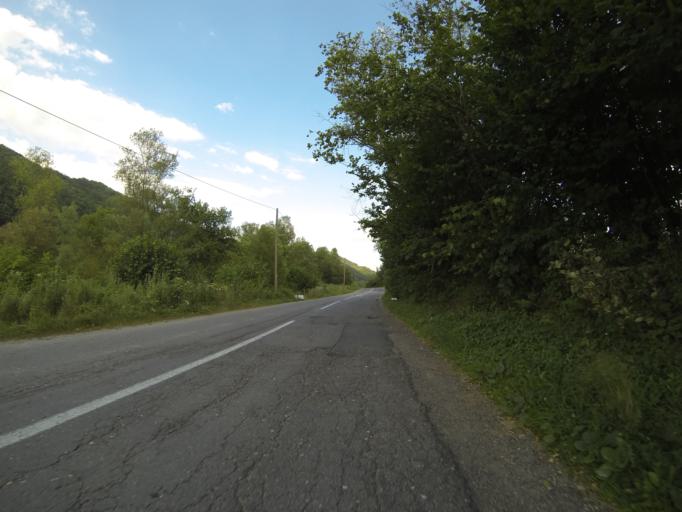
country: RO
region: Brasov
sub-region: Comuna Sinca Veche
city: Persani
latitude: 45.7380
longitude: 25.2257
